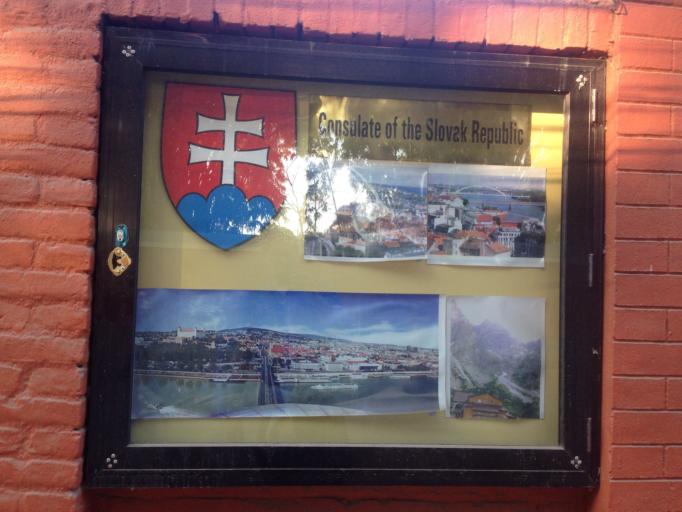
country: NP
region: Central Region
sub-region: Bagmati Zone
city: Kathmandu
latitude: 27.7177
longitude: 85.3242
